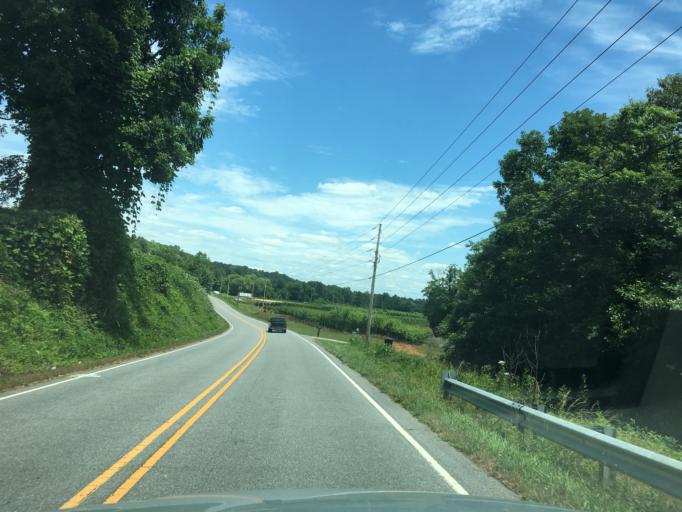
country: US
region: North Carolina
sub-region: Burke County
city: Glen Alpine
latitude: 35.6934
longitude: -81.7642
